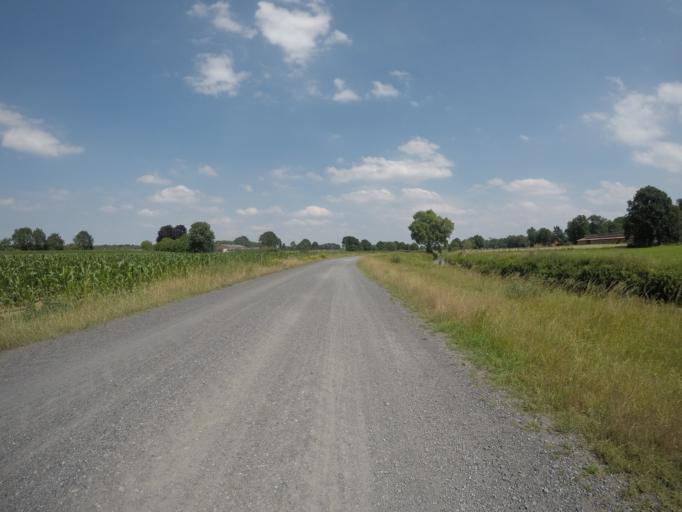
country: DE
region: North Rhine-Westphalia
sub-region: Regierungsbezirk Munster
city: Rhede
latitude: 51.8240
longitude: 6.7409
